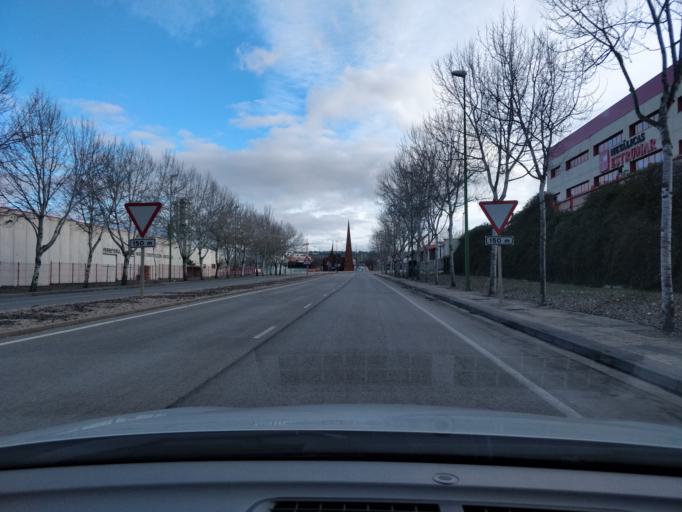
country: ES
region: Castille and Leon
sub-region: Provincia de Burgos
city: Sotragero
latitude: 42.3678
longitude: -3.7157
